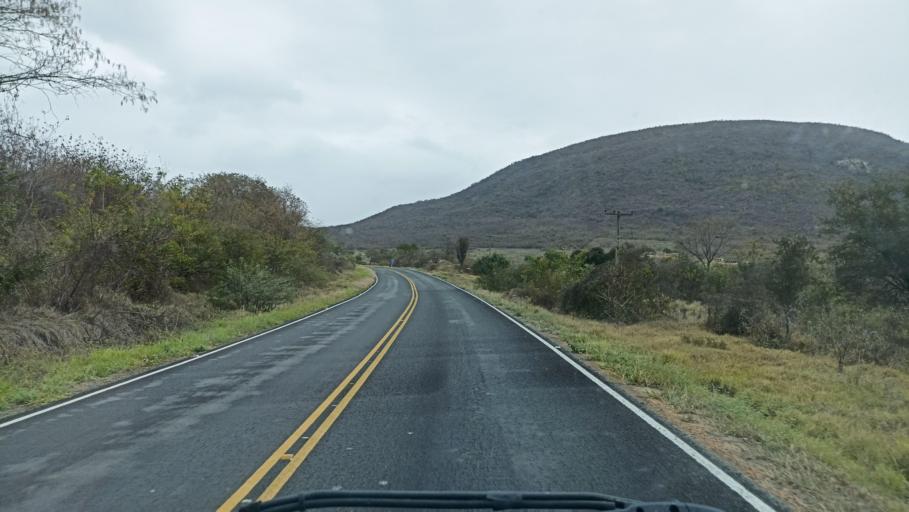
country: BR
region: Bahia
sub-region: Andarai
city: Vera Cruz
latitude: -13.0491
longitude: -40.7830
